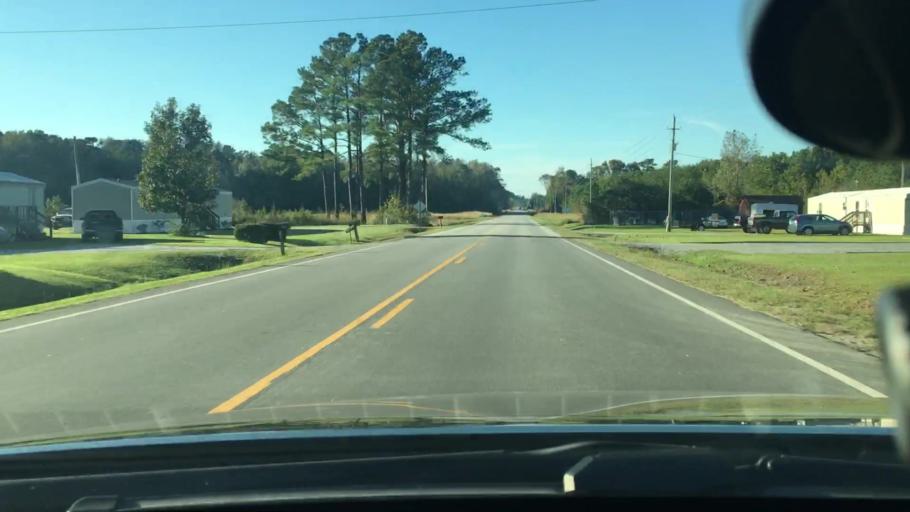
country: US
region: North Carolina
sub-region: Pitt County
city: Windsor
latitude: 35.4536
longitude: -77.2650
